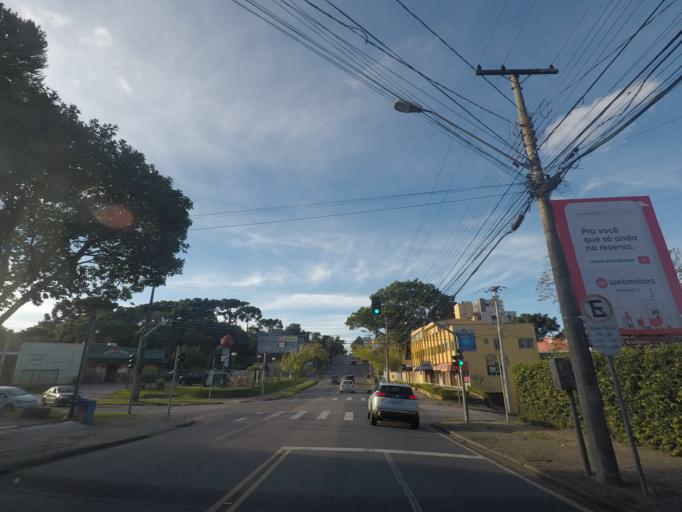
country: BR
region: Parana
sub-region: Curitiba
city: Curitiba
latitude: -25.4199
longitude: -49.2911
